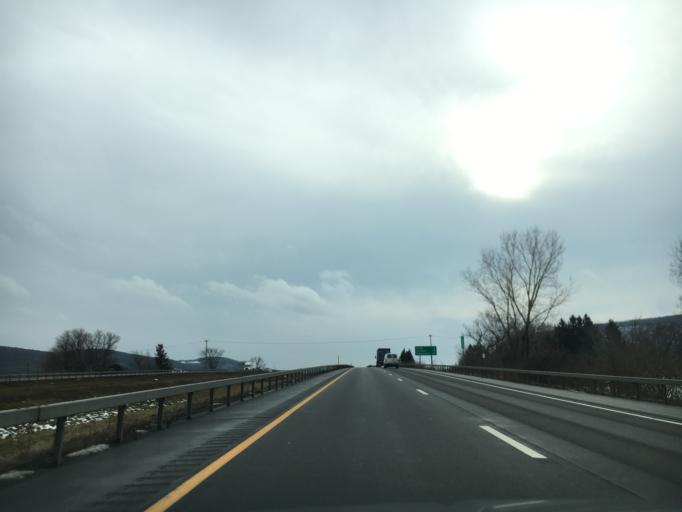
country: US
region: New York
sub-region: Cortland County
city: Homer
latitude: 42.7361
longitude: -76.1415
